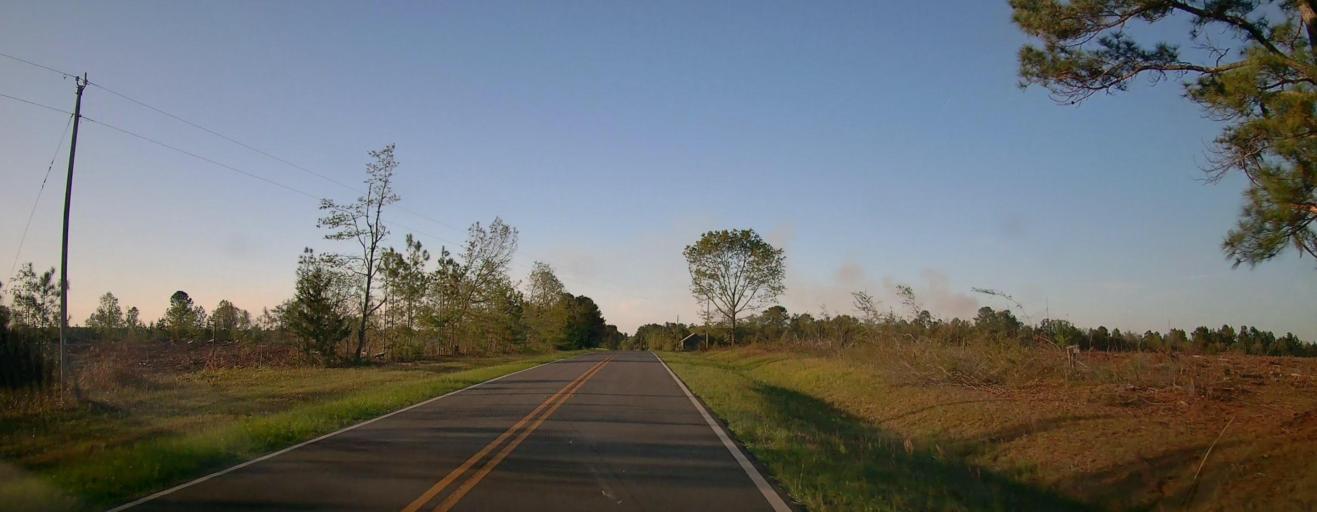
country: US
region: Georgia
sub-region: Marion County
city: Buena Vista
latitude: 32.4542
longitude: -84.4252
